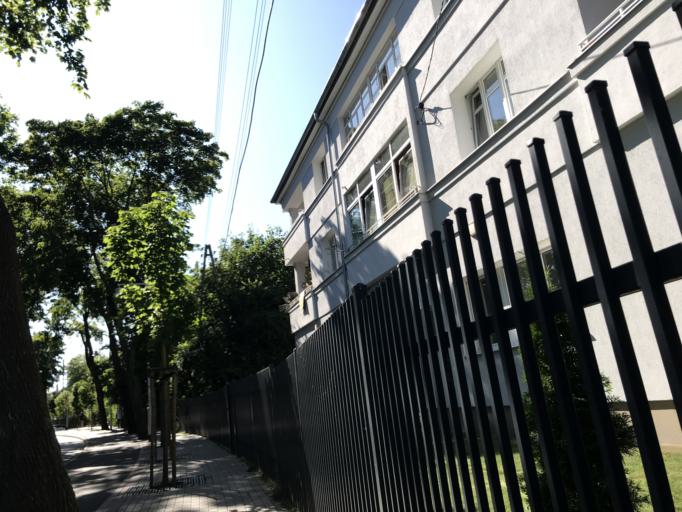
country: PL
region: Pomeranian Voivodeship
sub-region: Sopot
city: Sopot
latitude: 54.4802
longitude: 18.5583
